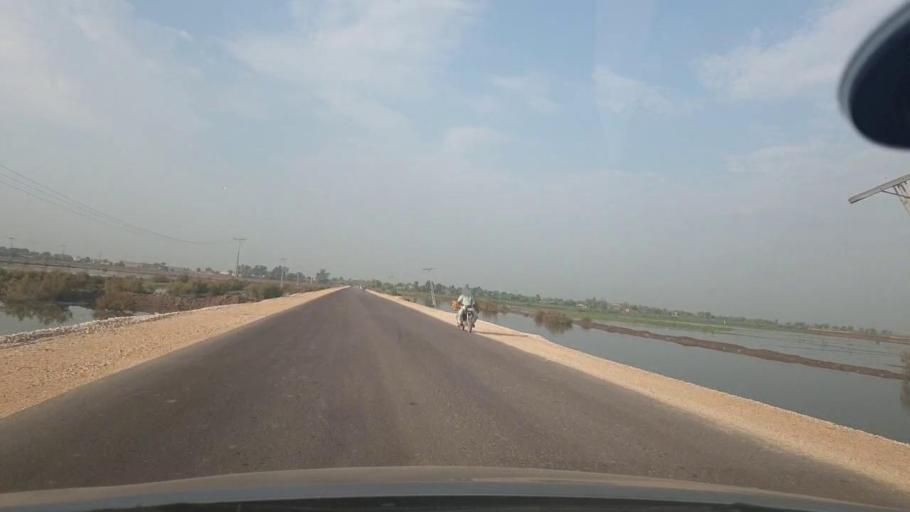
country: PK
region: Sindh
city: Jacobabad
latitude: 28.2214
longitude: 68.3742
